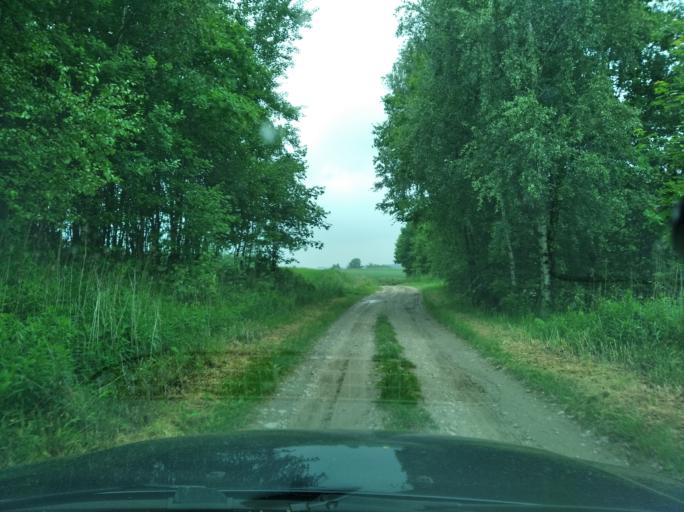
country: PL
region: Subcarpathian Voivodeship
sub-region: Powiat ropczycko-sedziszowski
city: Zagorzyce
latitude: 49.9839
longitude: 21.7063
